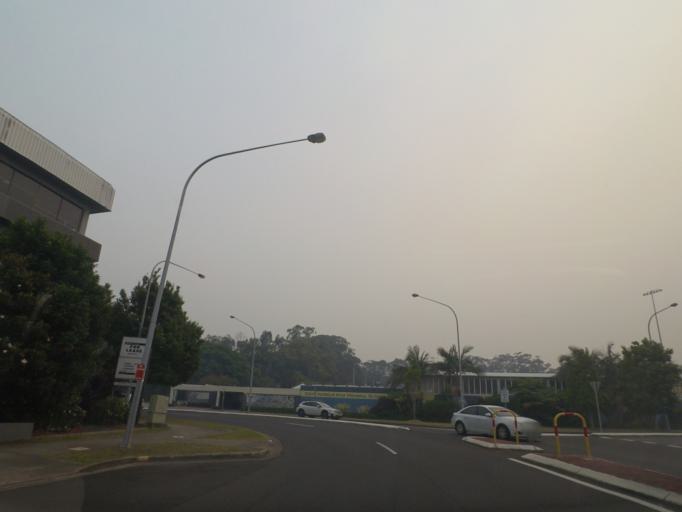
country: AU
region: New South Wales
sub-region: Coffs Harbour
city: Coffs Harbour
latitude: -30.2959
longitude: 153.1183
